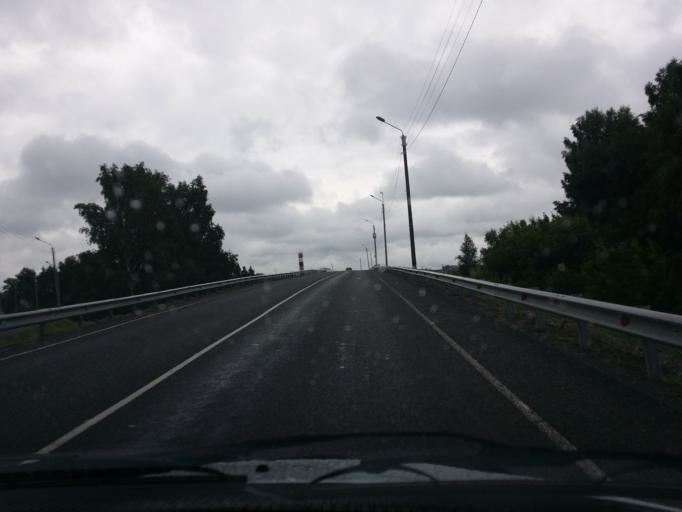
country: RU
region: Altai Krai
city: Vlasikha
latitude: 53.3550
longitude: 83.5522
